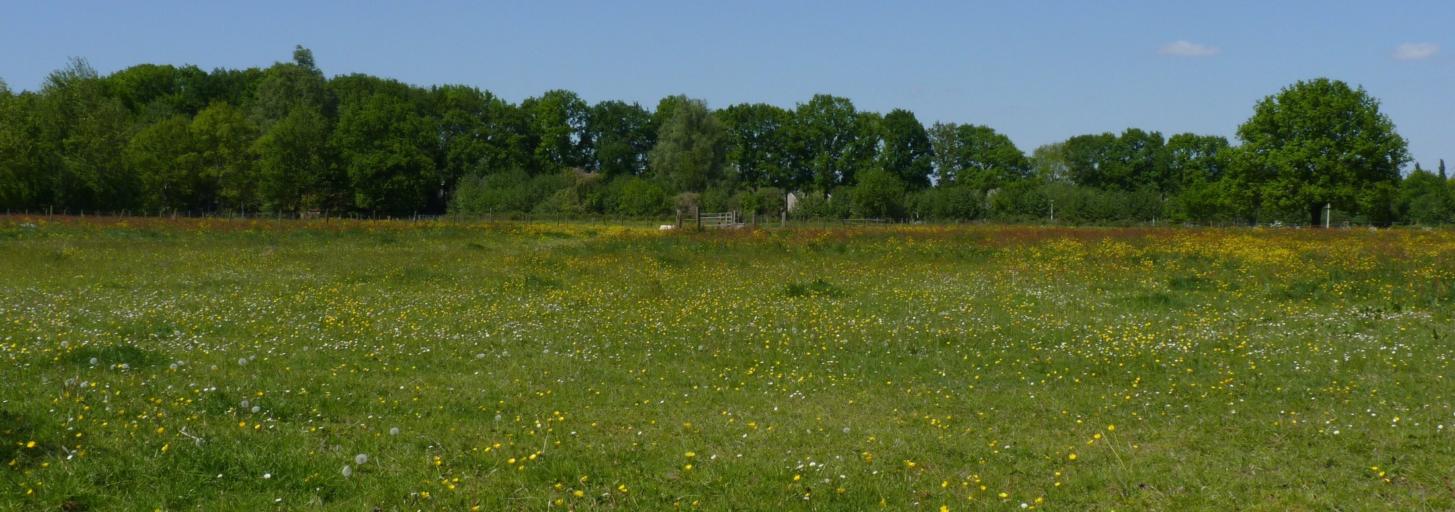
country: NL
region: Utrecht
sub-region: Gemeente Amersfoort
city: Hoogland
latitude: 52.1787
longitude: 5.3827
